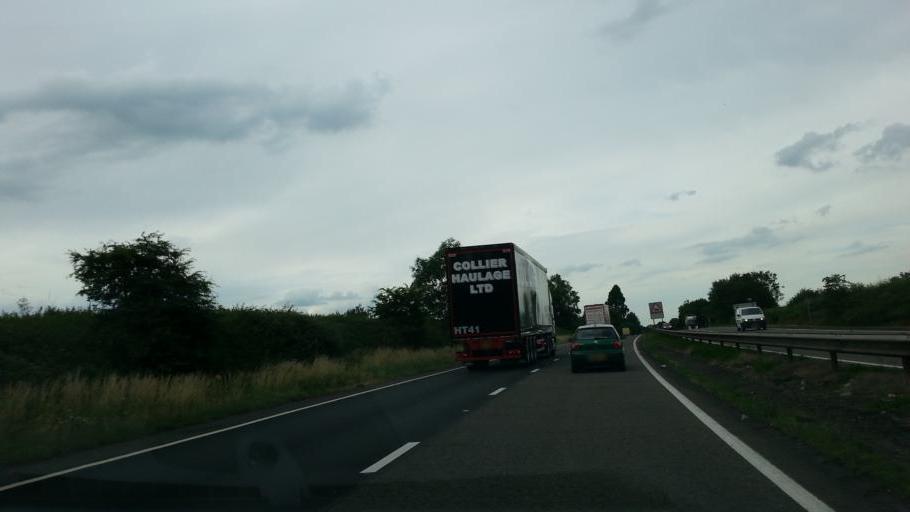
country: GB
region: England
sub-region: Herefordshire
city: Walford
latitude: 51.9066
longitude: -2.6226
